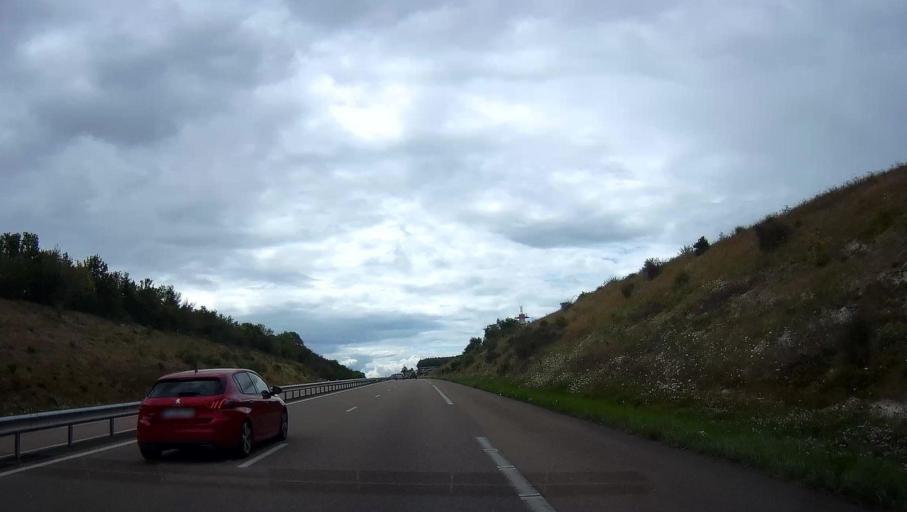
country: FR
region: Champagne-Ardenne
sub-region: Departement de l'Aube
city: Creney-pres-Troyes
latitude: 48.3748
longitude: 4.1576
